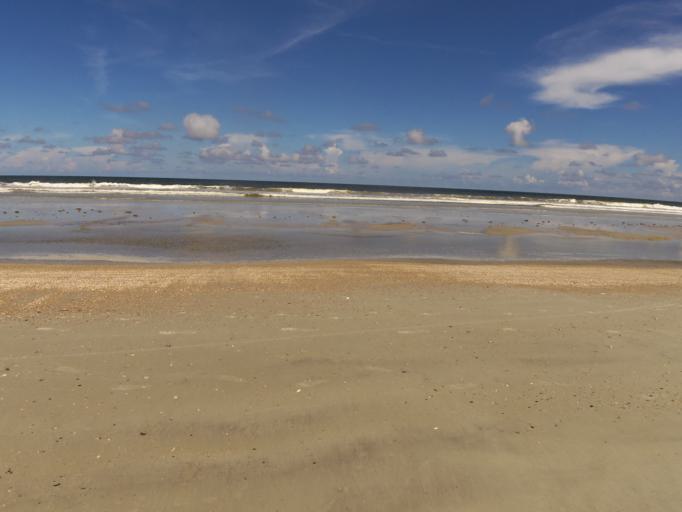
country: US
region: Florida
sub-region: Duval County
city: Atlantic Beach
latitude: 30.4704
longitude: -81.4123
